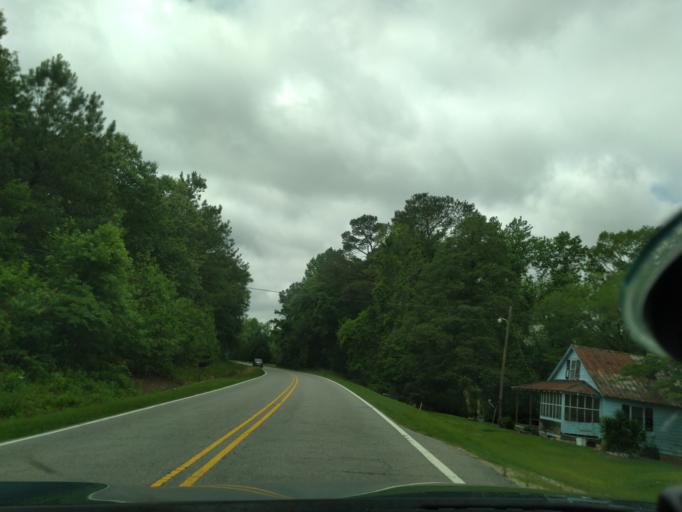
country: US
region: North Carolina
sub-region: Washington County
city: Plymouth
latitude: 35.9004
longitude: -76.6900
